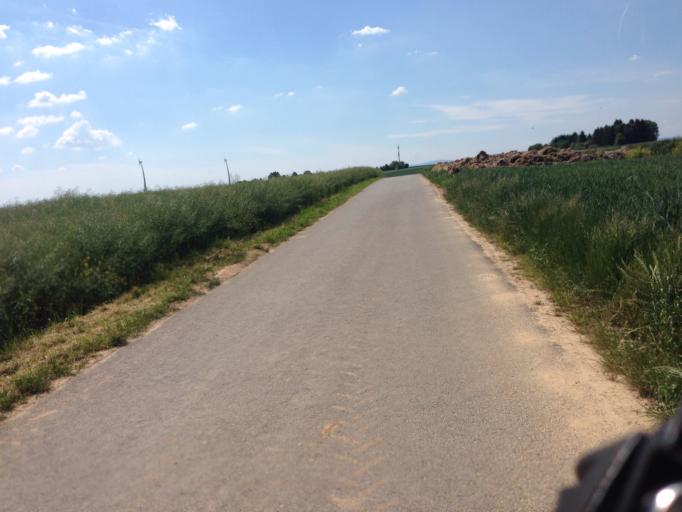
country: DE
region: Hesse
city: Bruchkobel
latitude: 50.2155
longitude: 8.9047
